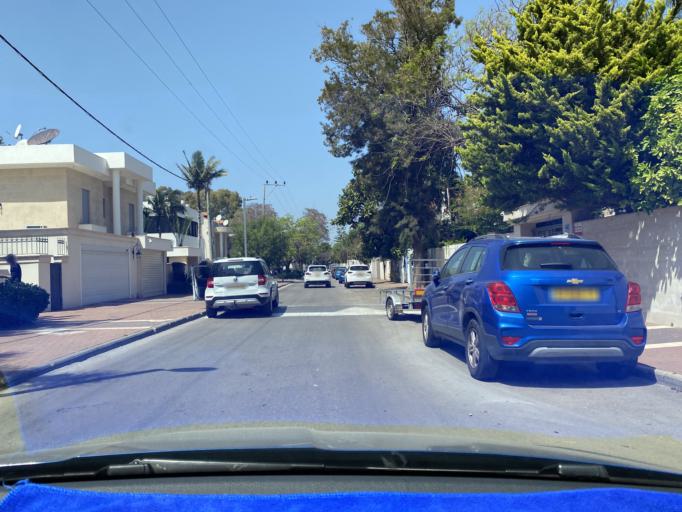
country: IL
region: Tel Aviv
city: Kefar Shemaryahu
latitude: 32.1775
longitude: 34.8145
